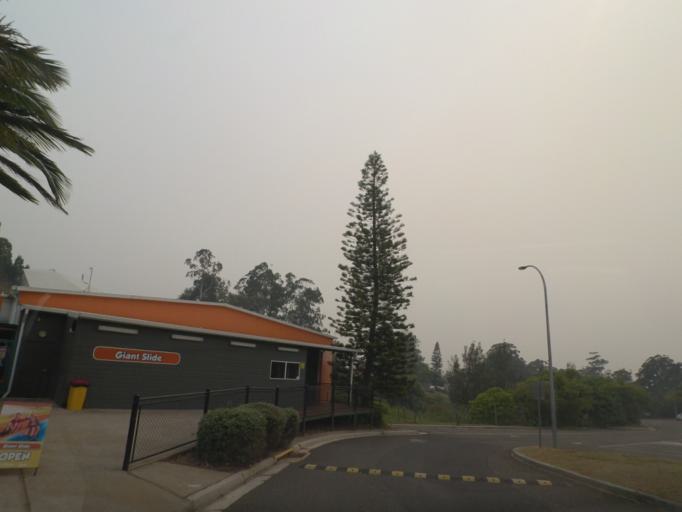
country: AU
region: New South Wales
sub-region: Coffs Harbour
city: Coffs Harbour
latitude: -30.2740
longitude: 153.1315
